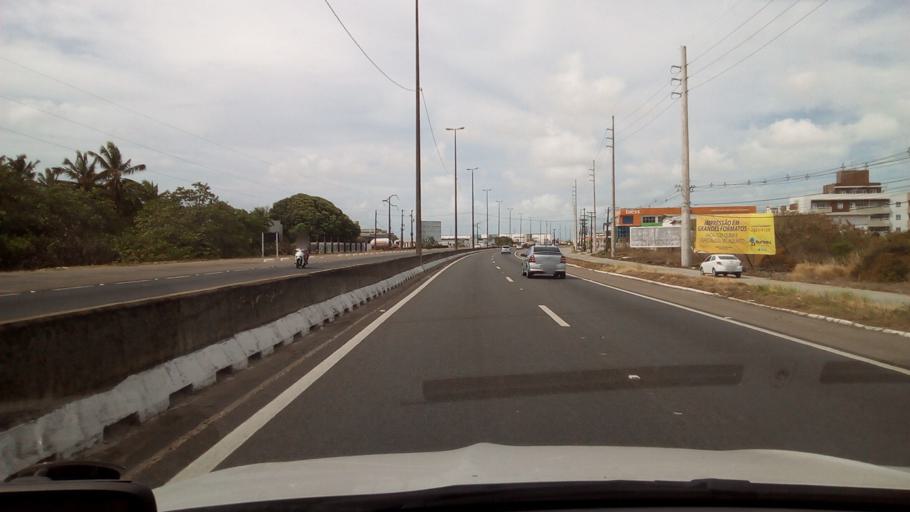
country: BR
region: Paraiba
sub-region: Joao Pessoa
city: Joao Pessoa
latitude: -7.0566
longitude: -34.8507
